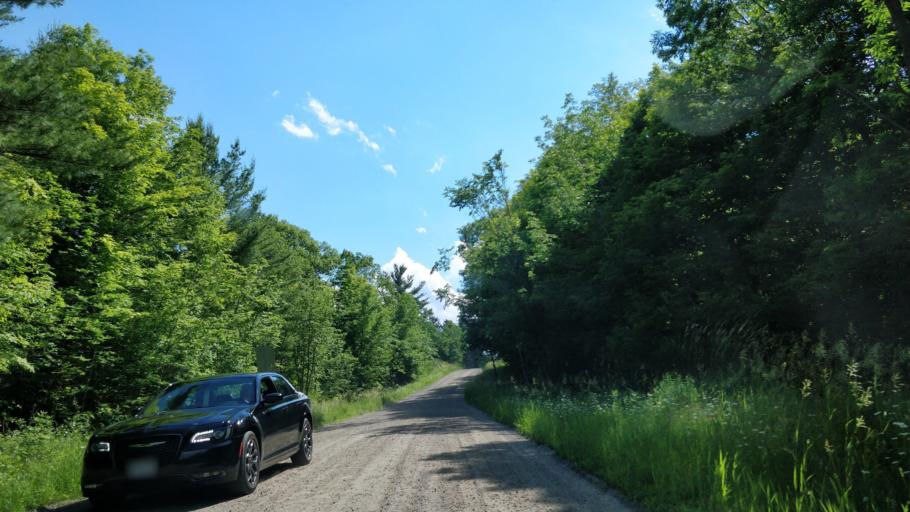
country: CA
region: Ontario
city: Perth
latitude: 44.7232
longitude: -76.5143
